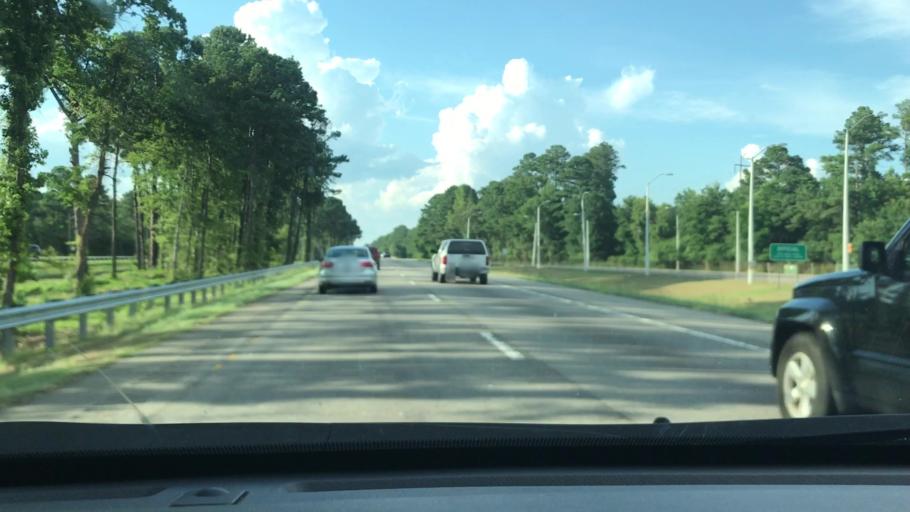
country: US
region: North Carolina
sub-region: Robeson County
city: Lumberton
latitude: 34.7060
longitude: -78.9977
